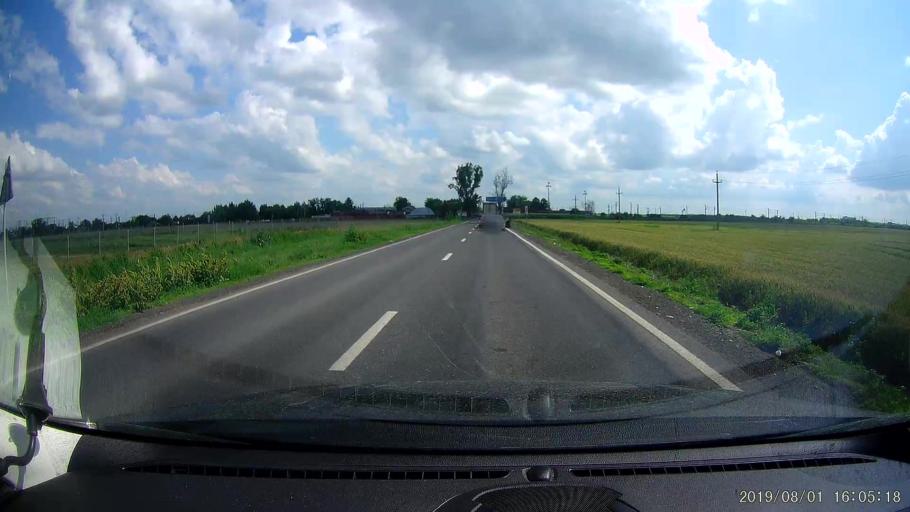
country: RO
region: Calarasi
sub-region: Comuna Dragalina
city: Drajna Noua
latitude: 44.4294
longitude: 27.3769
